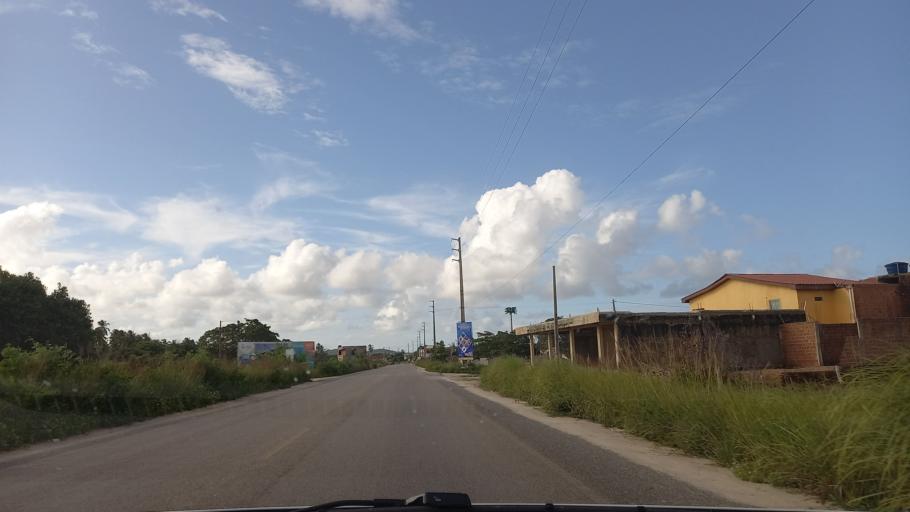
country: BR
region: Pernambuco
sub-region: Tamandare
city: Tamandare
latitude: -8.7347
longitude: -35.0959
